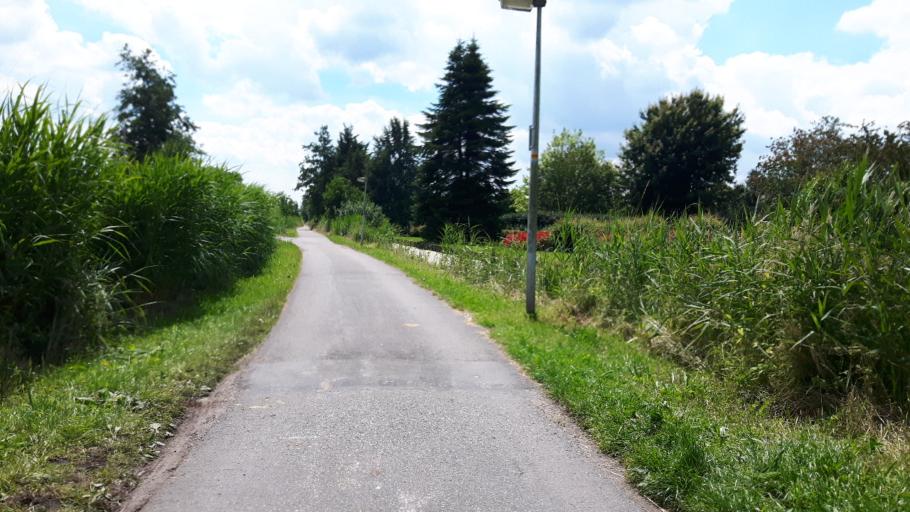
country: NL
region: South Holland
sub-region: Gemeente Boskoop
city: Boskoop
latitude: 52.0842
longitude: 4.6901
